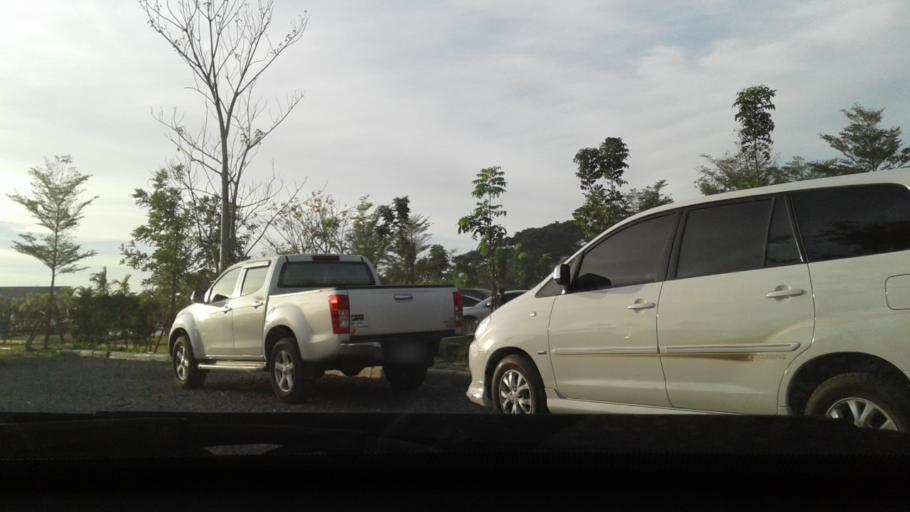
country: TH
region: Nakhon Pathom
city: Nakhon Chai Si
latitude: 13.8987
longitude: 100.2347
